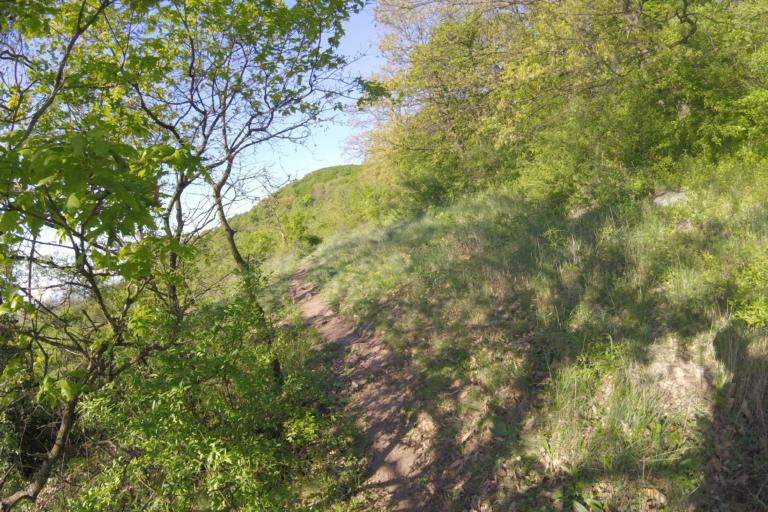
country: HU
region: Heves
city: Abasar
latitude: 47.8013
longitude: 19.9857
